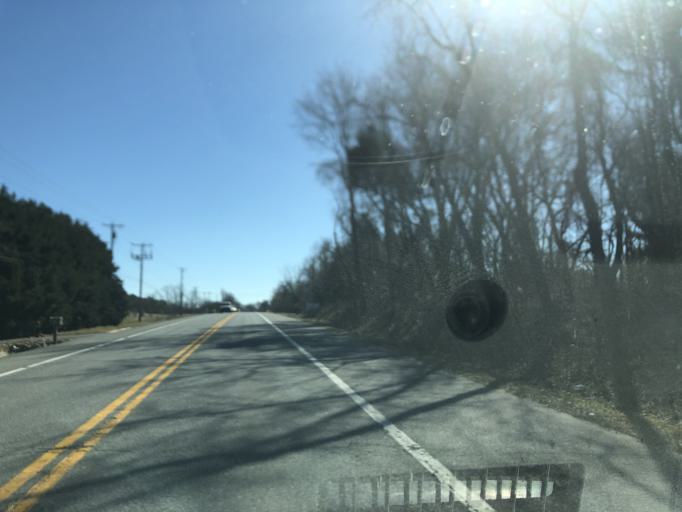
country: US
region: Maryland
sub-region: Calvert County
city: Dunkirk
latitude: 38.7878
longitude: -76.6445
